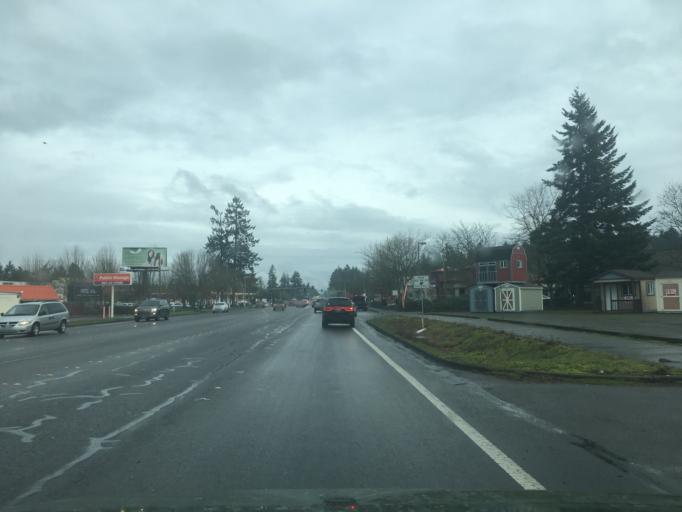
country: US
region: Washington
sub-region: Thurston County
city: Tanglewilde-Thompson Place
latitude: 47.0561
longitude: -122.7674
